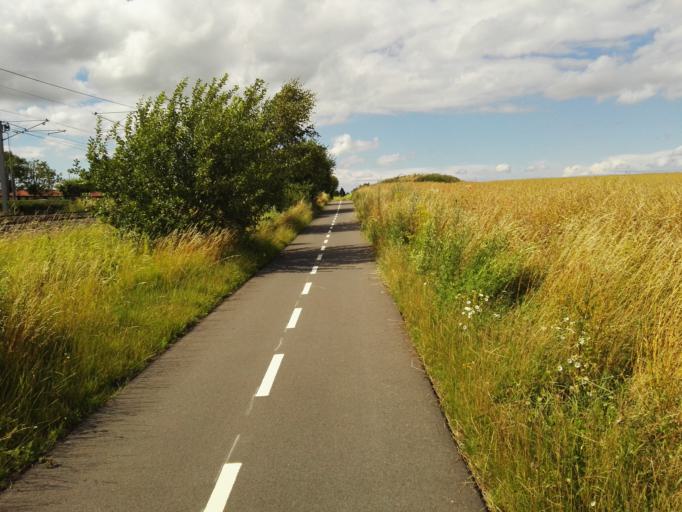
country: DK
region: Capital Region
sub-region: Egedal Kommune
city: Stenlose
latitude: 55.7841
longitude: 12.1835
